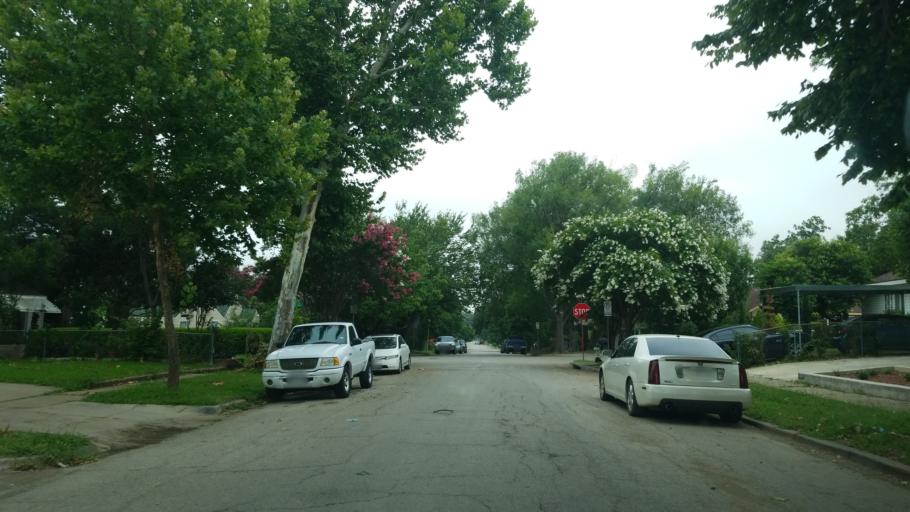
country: US
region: Texas
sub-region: Dallas County
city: University Park
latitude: 32.8379
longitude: -96.8597
